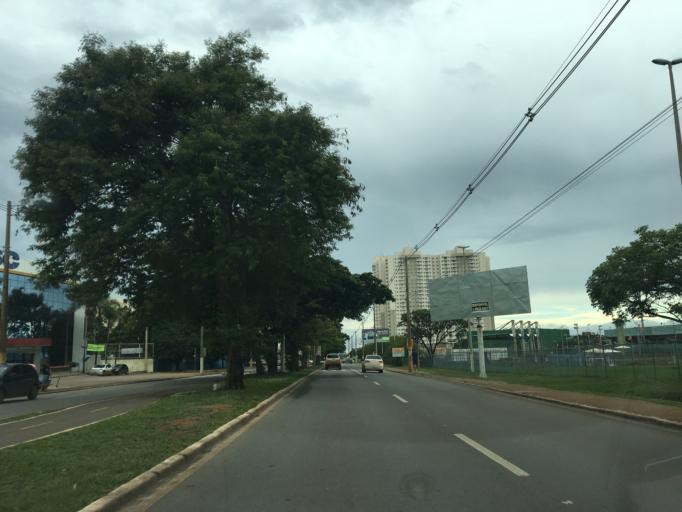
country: BR
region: Federal District
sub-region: Brasilia
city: Brasilia
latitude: -16.0096
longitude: -48.0599
